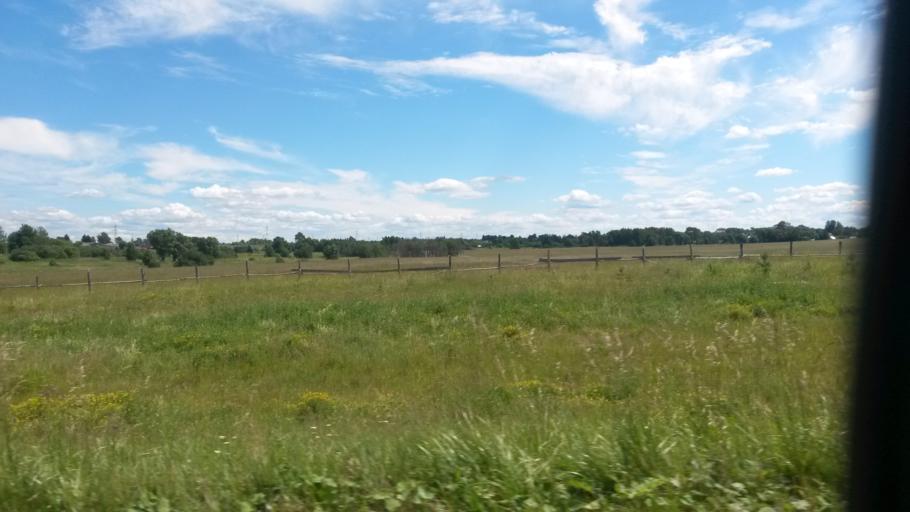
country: RU
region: Ivanovo
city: Staraya Vichuga
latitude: 57.2348
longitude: 41.8763
